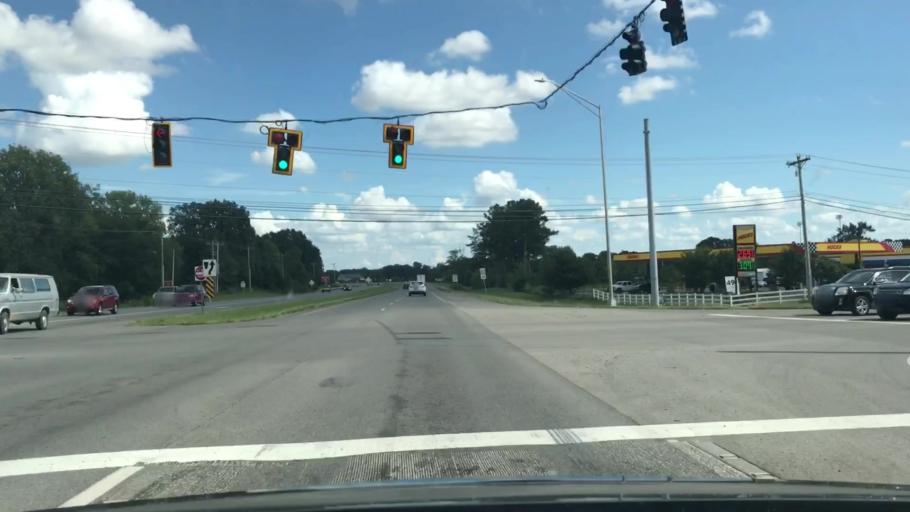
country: US
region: Kentucky
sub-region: Christian County
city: Hopkinsville
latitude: 36.8217
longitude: -87.5049
